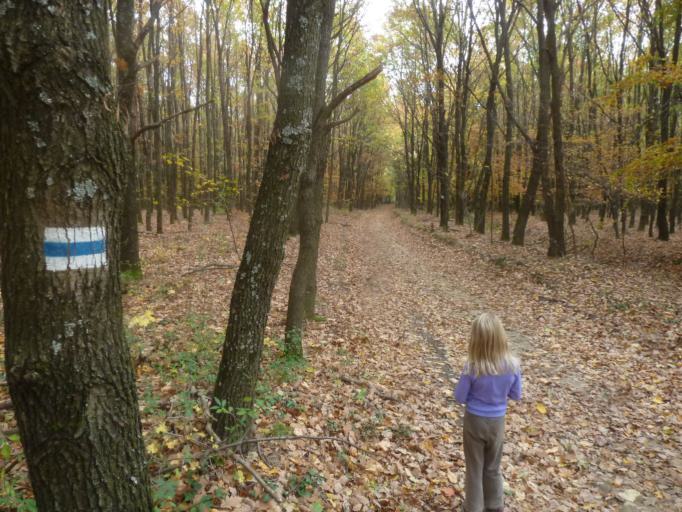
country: HU
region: Zala
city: Pacsa
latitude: 46.5919
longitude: 17.0521
